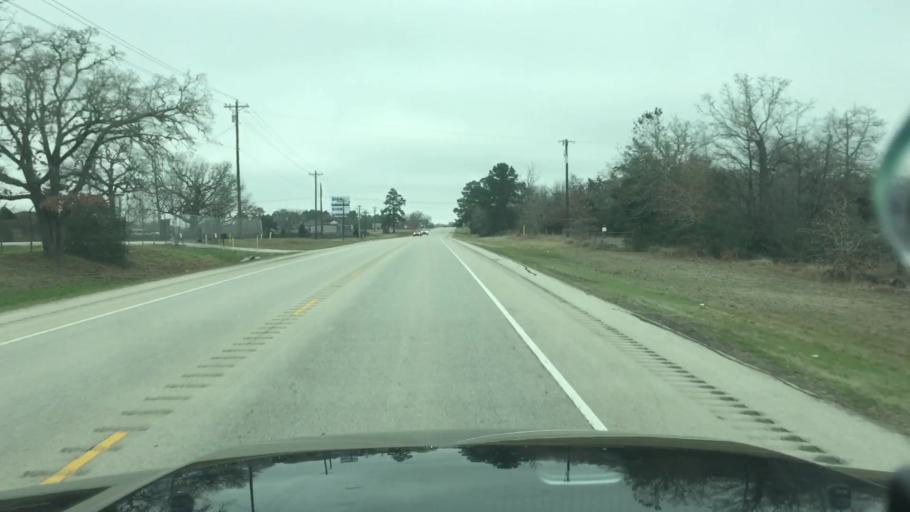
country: US
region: Texas
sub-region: Lee County
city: Giddings
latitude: 30.0491
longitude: -96.9142
